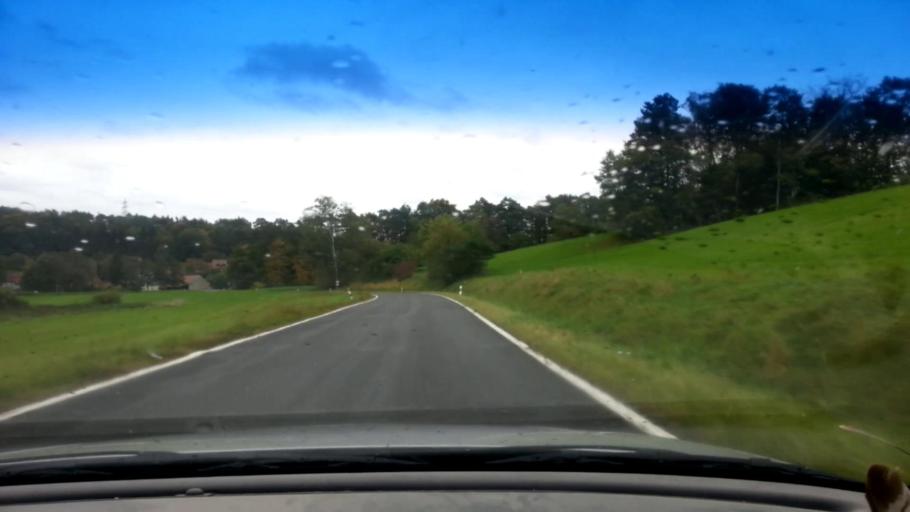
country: DE
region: Bavaria
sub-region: Regierungsbezirk Unterfranken
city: Kirchlauter
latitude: 50.0270
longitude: 10.7334
